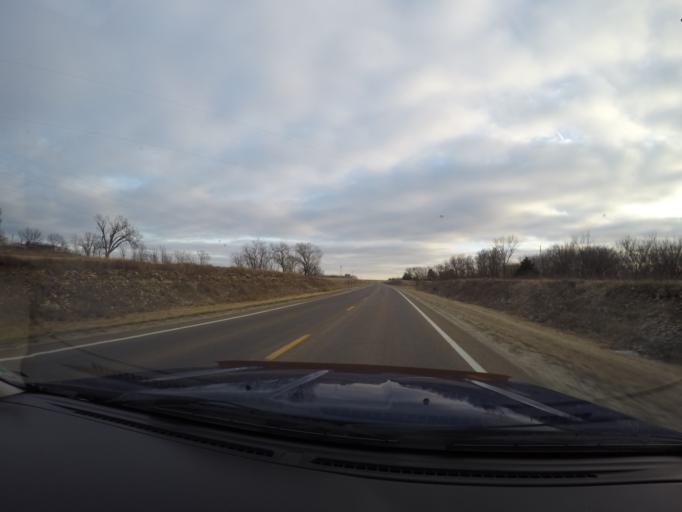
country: US
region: Kansas
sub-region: Morris County
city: Council Grove
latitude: 38.6952
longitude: -96.4952
